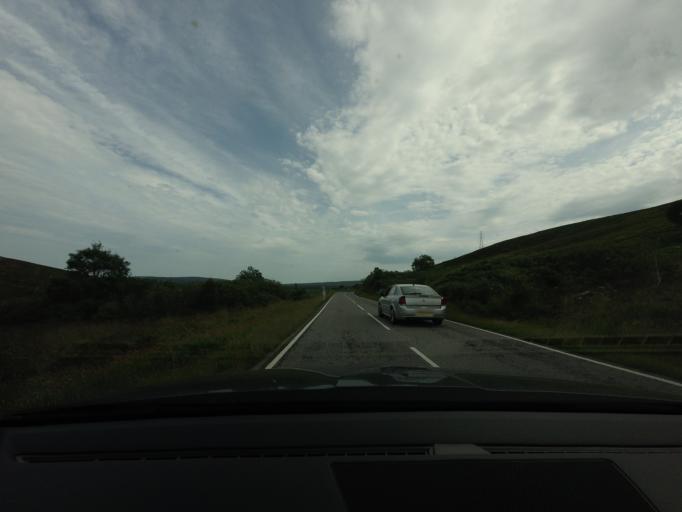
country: GB
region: Scotland
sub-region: Highland
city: Alness
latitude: 57.8256
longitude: -4.2646
